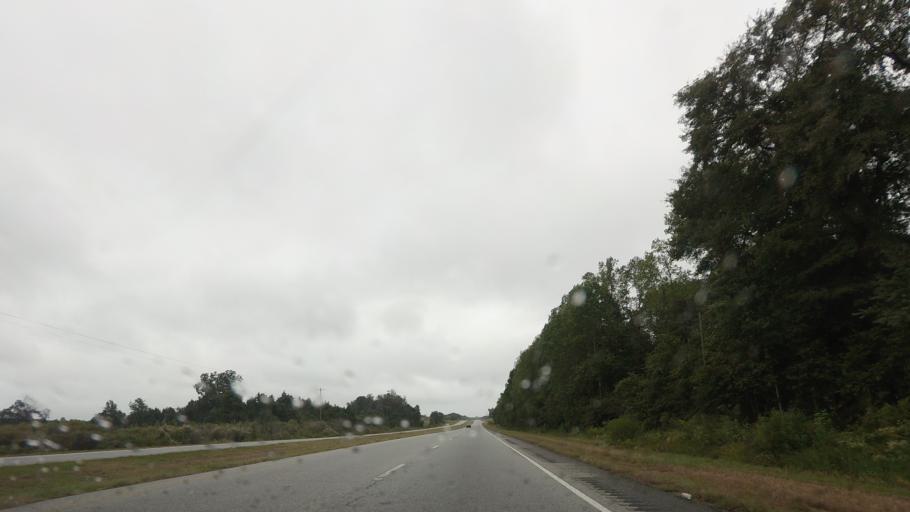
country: US
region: Georgia
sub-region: Lowndes County
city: Valdosta
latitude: 30.8236
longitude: -83.2287
